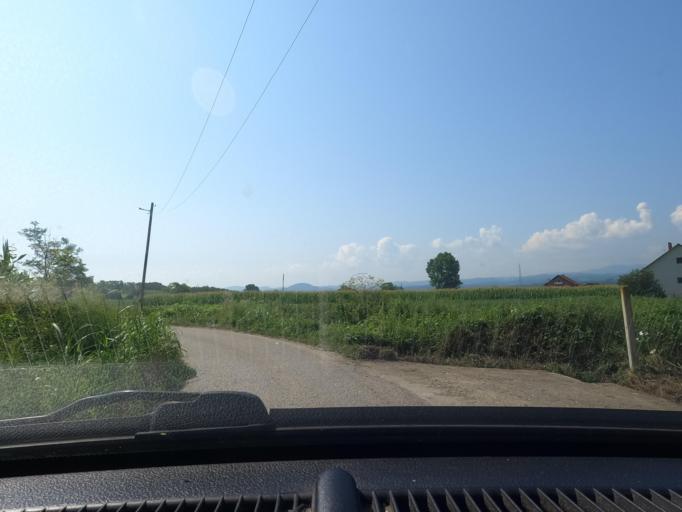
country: RS
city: Jadranska Lesnica
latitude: 44.5436
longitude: 19.3677
